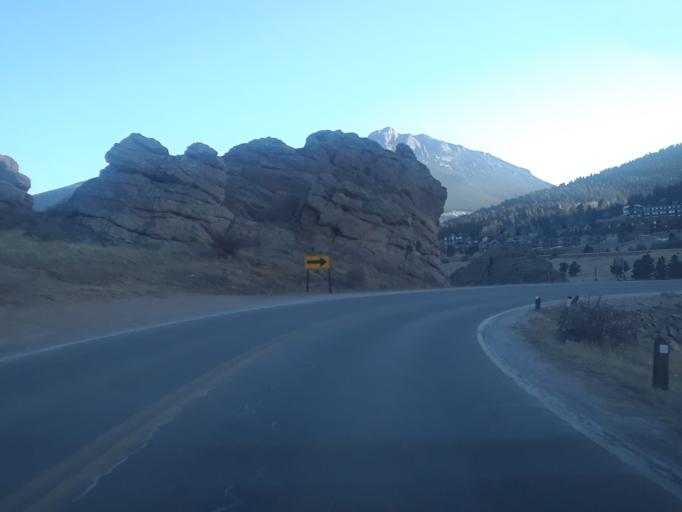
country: US
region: Colorado
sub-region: Larimer County
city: Estes Park
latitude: 40.3431
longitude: -105.5295
